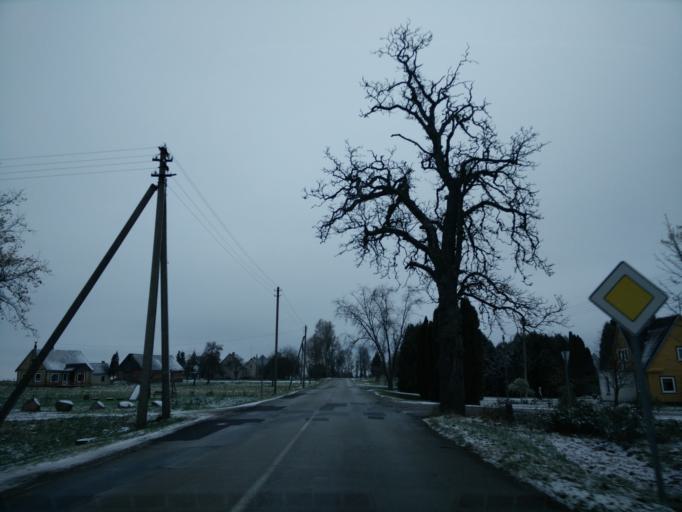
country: LT
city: Ariogala
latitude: 55.4219
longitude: 23.3465
